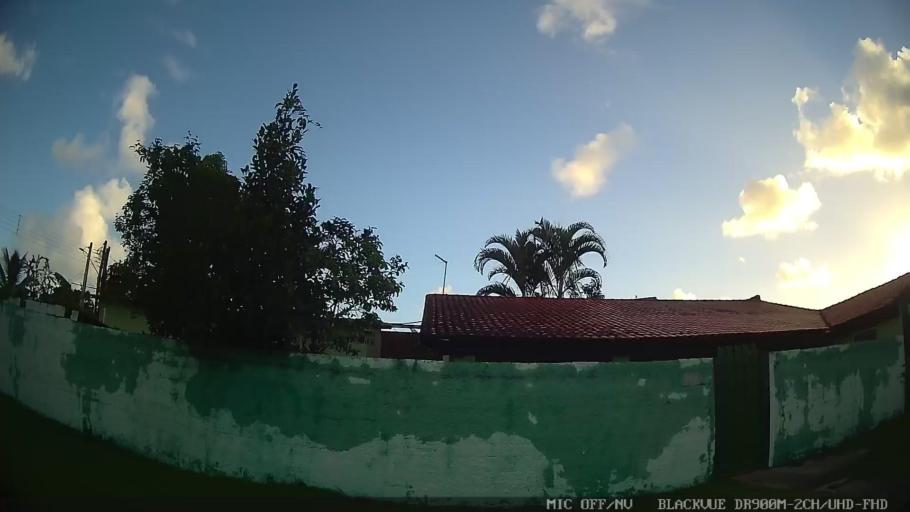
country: BR
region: Sao Paulo
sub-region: Itanhaem
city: Itanhaem
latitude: -24.1420
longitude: -46.7308
